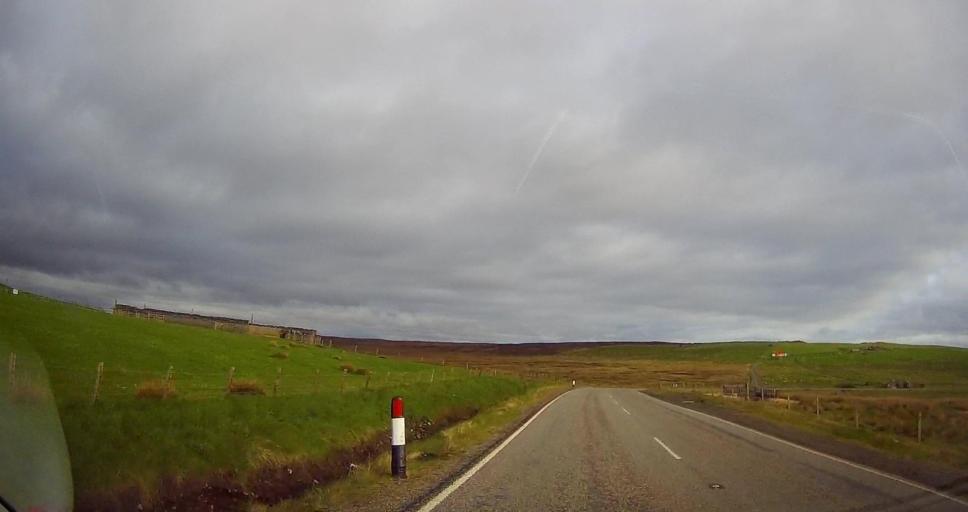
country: GB
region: Scotland
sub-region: Shetland Islands
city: Lerwick
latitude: 60.4637
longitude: -1.2114
